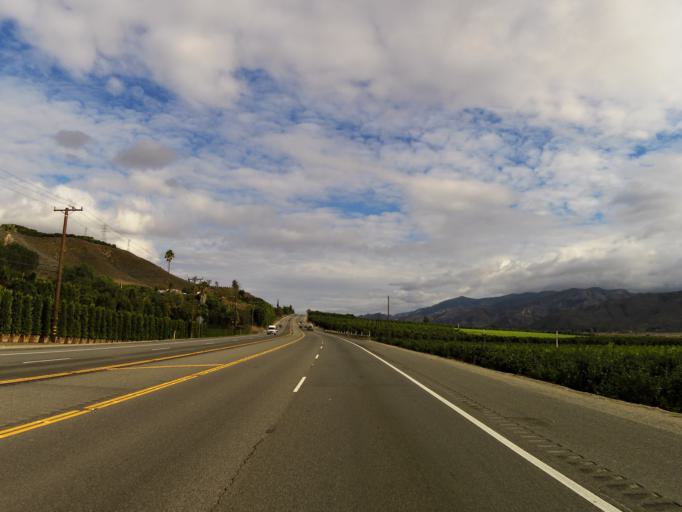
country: US
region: California
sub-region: Ventura County
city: Fillmore
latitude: 34.3955
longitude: -118.8741
